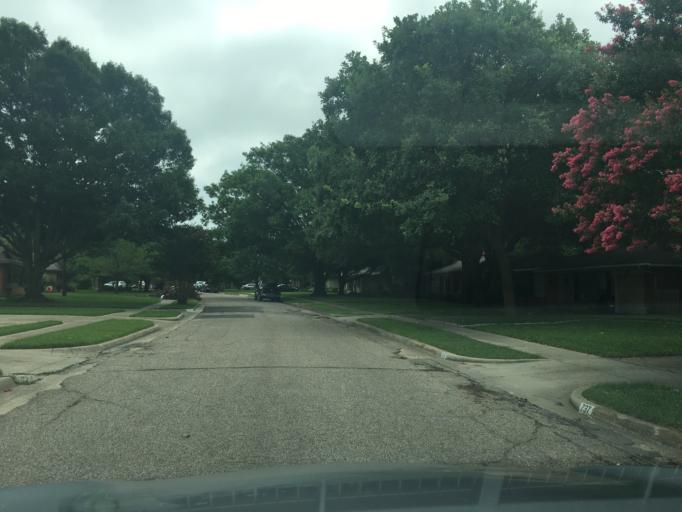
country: US
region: Texas
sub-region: Dallas County
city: Richardson
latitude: 32.9484
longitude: -96.7480
